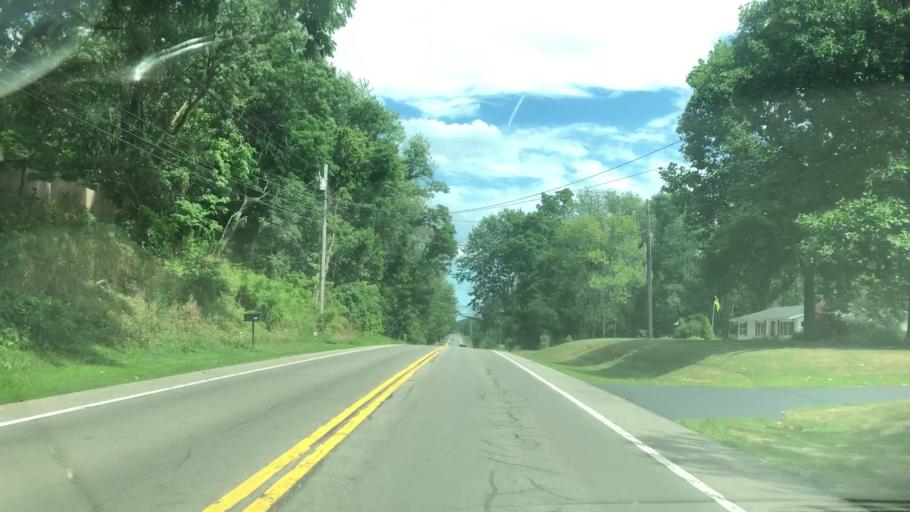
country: US
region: New York
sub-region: Monroe County
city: Webster
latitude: 43.1598
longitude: -77.4215
